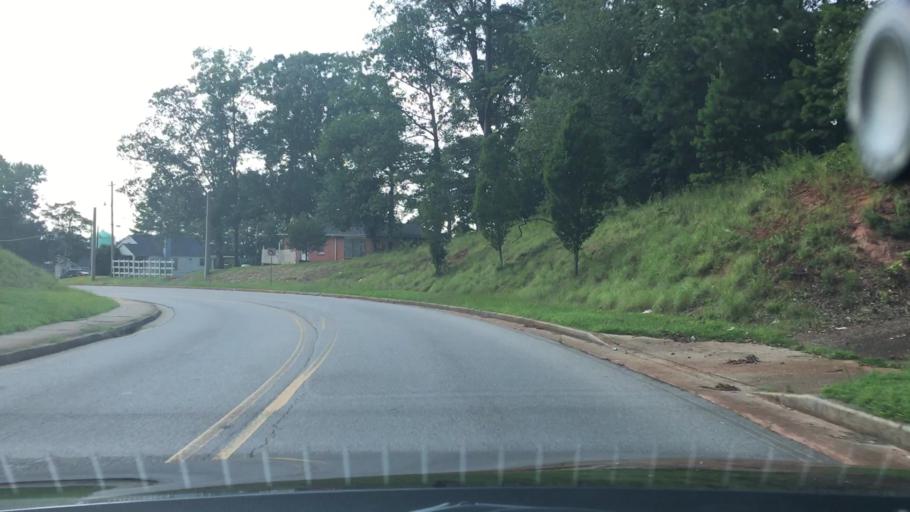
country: US
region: Georgia
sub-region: Spalding County
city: Experiment
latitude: 33.2497
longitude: -84.2854
